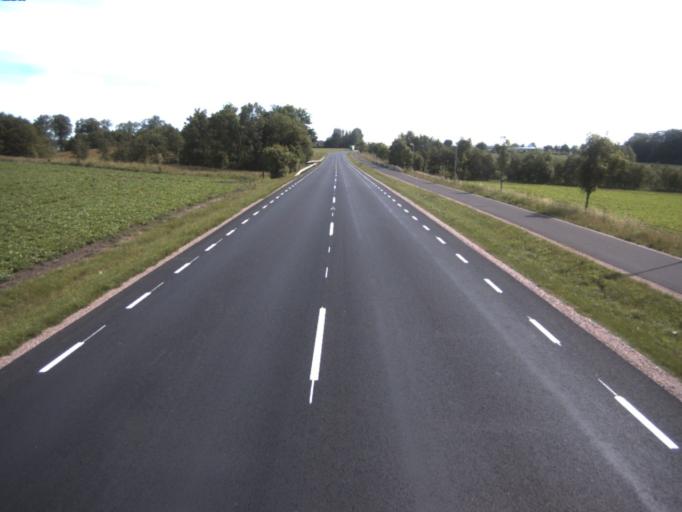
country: SE
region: Skane
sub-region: Helsingborg
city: Barslov
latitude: 56.0417
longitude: 12.7699
